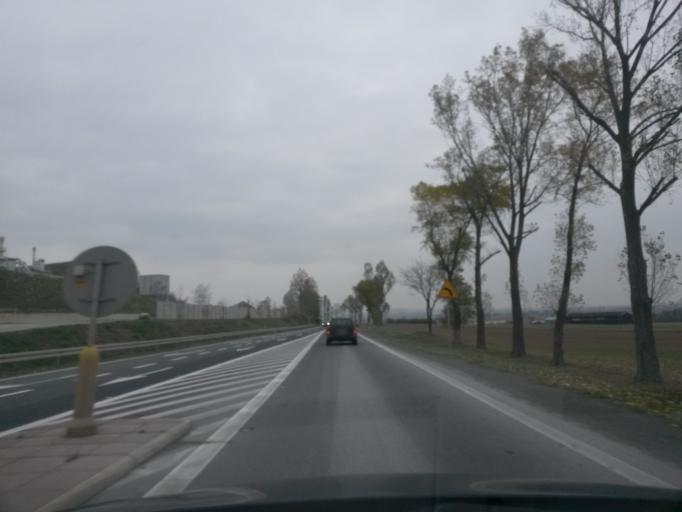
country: PL
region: Lower Silesian Voivodeship
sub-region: Powiat zabkowicki
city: Zabkowice Slaskie
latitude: 50.5411
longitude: 16.7955
